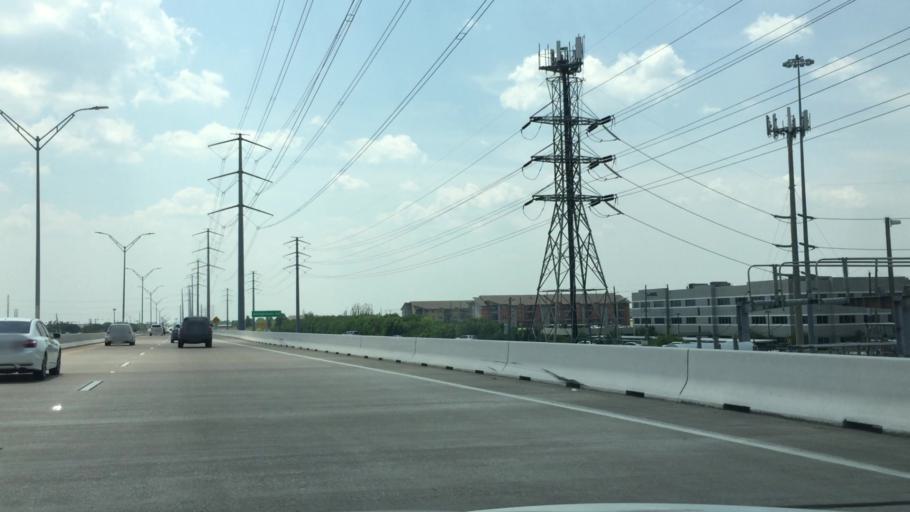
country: US
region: Texas
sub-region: Harris County
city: Bunker Hill Village
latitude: 29.7183
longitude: -95.5585
